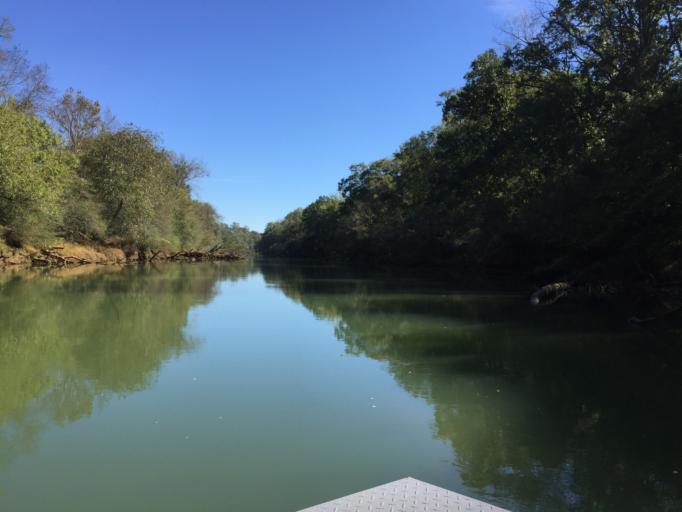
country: US
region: Georgia
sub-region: Gwinnett County
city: Duluth
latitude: 34.0311
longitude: -84.1353
